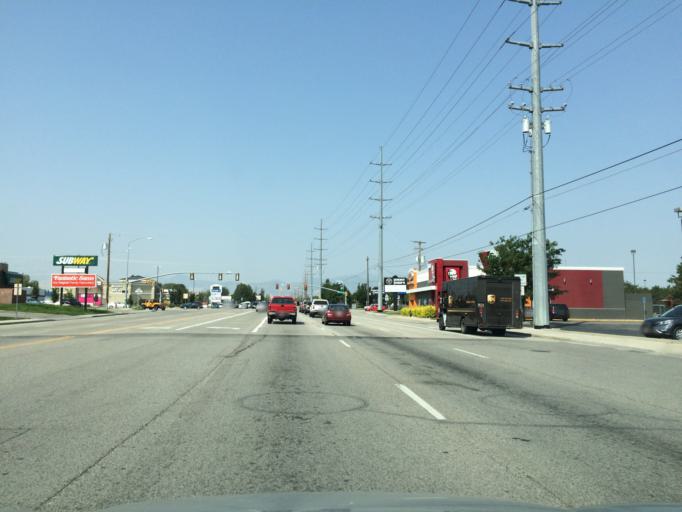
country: US
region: Utah
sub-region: Salt Lake County
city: West Jordan
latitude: 40.5878
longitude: -111.9371
